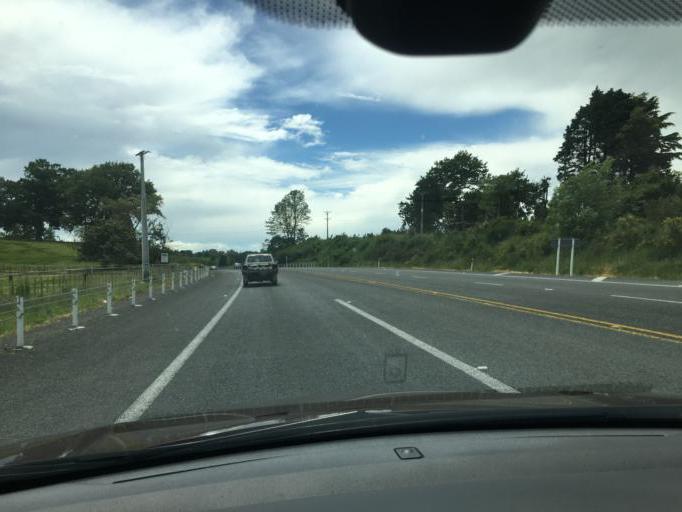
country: NZ
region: Waikato
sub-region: Waipa District
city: Cambridge
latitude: -37.9564
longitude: 175.3185
